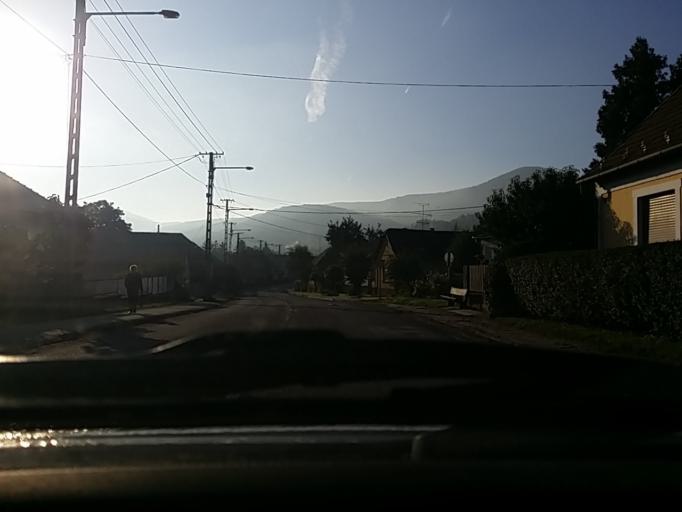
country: HU
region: Komarom-Esztergom
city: Pilismarot
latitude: 47.7673
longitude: 18.9043
